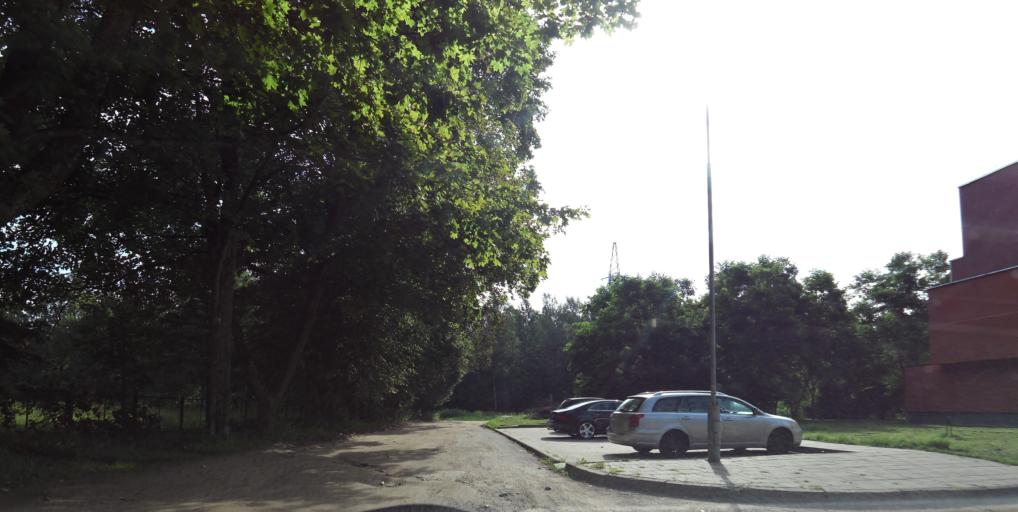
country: LT
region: Vilnius County
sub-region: Vilnius
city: Fabijoniskes
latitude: 54.7392
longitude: 25.2821
